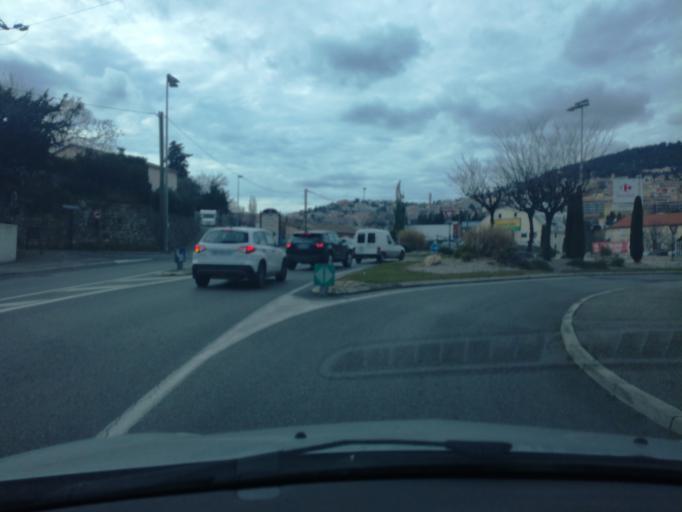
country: FR
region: Provence-Alpes-Cote d'Azur
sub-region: Departement des Alpes-Maritimes
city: Grasse
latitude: 43.6552
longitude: 6.9399
